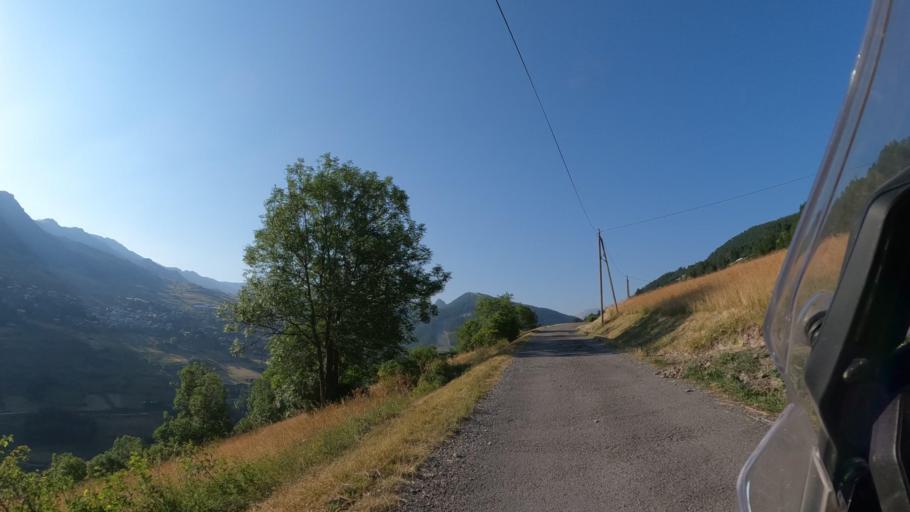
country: FR
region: Provence-Alpes-Cote d'Azur
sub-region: Departement des Hautes-Alpes
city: Guillestre
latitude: 44.6067
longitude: 6.6818
